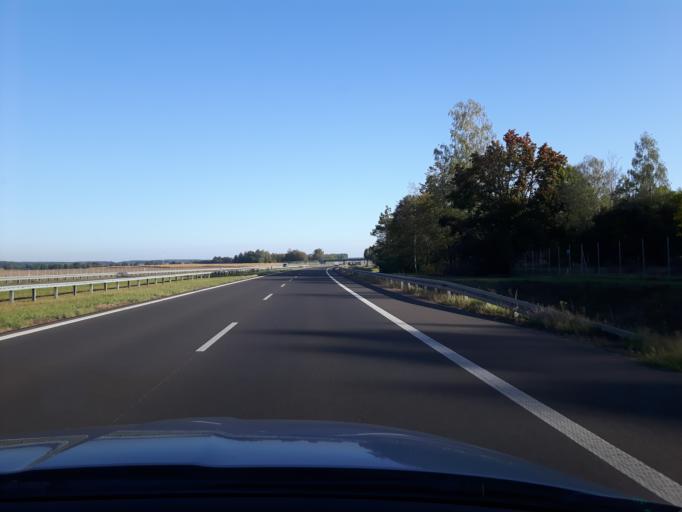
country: PL
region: Masovian Voivodeship
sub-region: Powiat mlawski
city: Wieczfnia Koscielna
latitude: 53.2574
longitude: 20.4257
